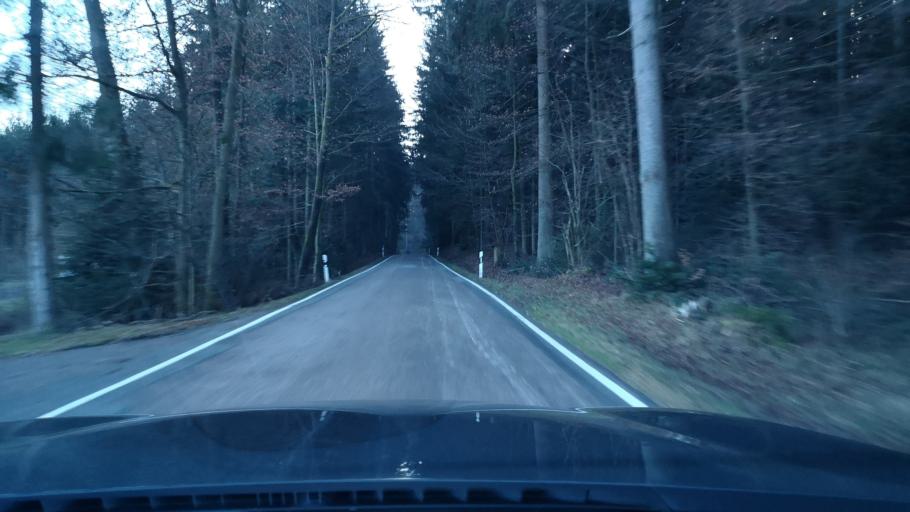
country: DE
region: Baden-Wuerttemberg
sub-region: Regierungsbezirk Stuttgart
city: Gschwend
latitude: 48.9415
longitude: 9.7008
